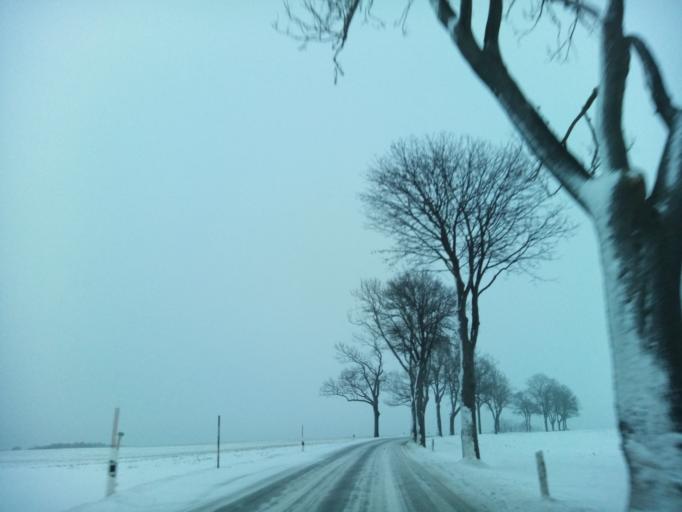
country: DE
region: Saxony
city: Eppendorf
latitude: 50.8245
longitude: 13.2792
